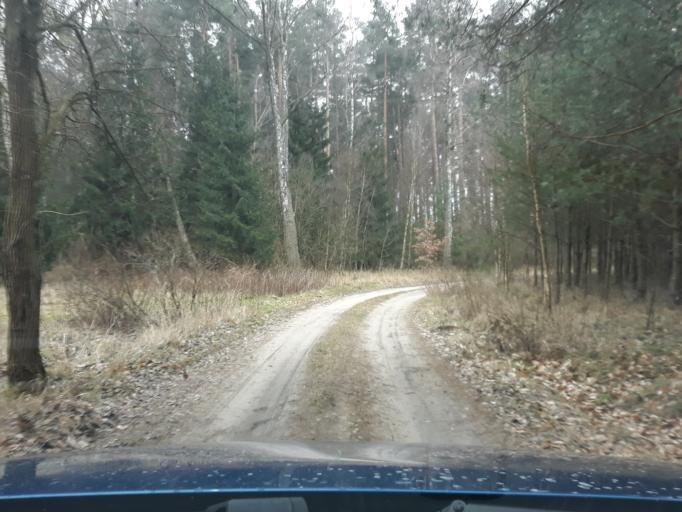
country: PL
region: Pomeranian Voivodeship
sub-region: Powiat czluchowski
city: Czluchow
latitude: 53.8238
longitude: 17.4267
